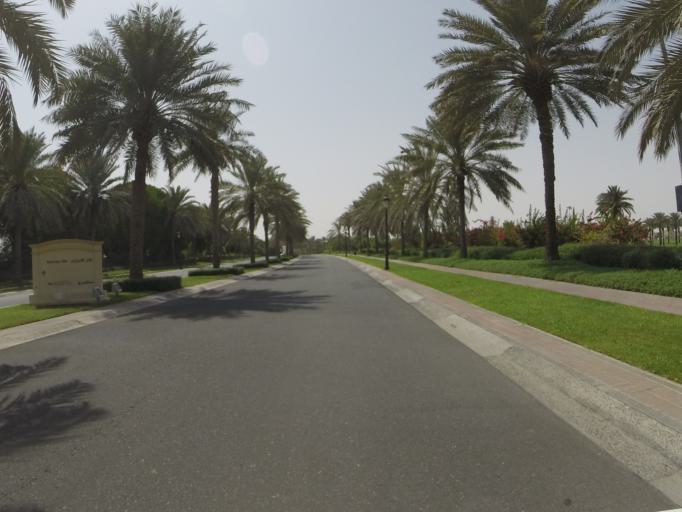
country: AE
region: Dubai
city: Dubai
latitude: 25.0706
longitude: 55.1601
